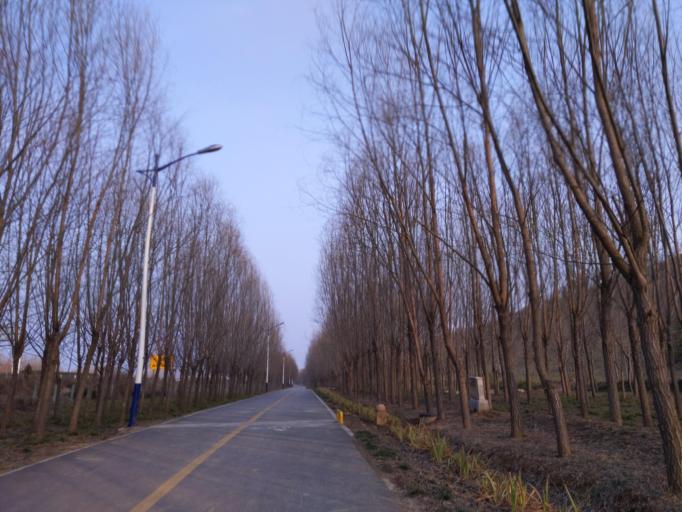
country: CN
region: Henan Sheng
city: Puyang
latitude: 35.8210
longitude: 115.0014
